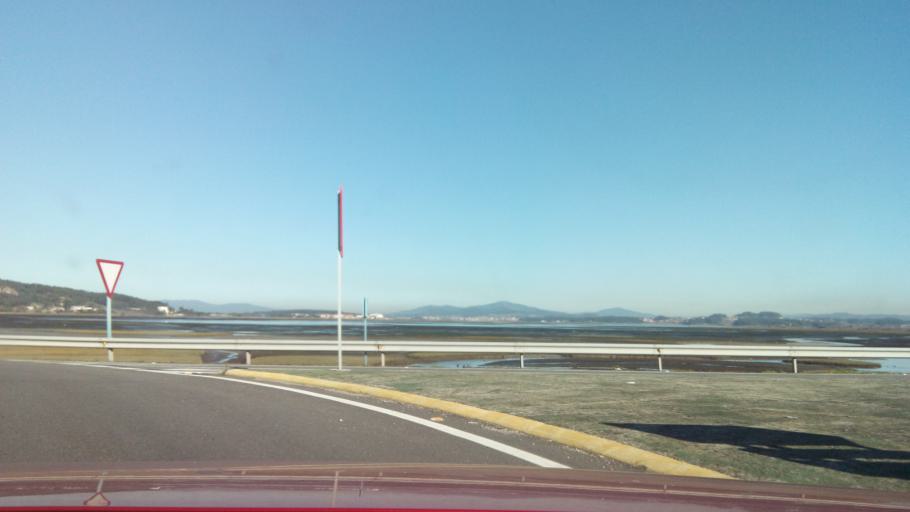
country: ES
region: Galicia
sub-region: Provincia de Pontevedra
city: O Grove
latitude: 42.4476
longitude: -8.8692
